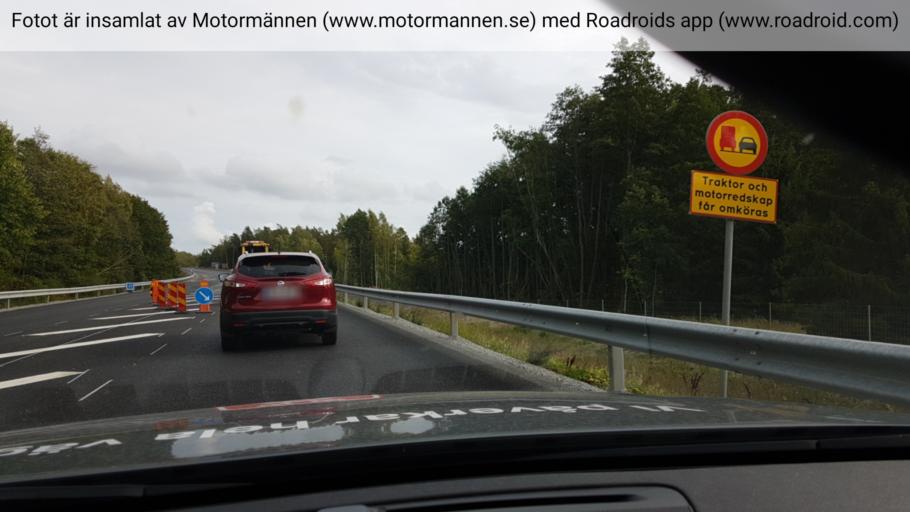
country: SE
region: Stockholm
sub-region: Norrtalje Kommun
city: Bjorko
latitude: 59.7199
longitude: 18.9193
